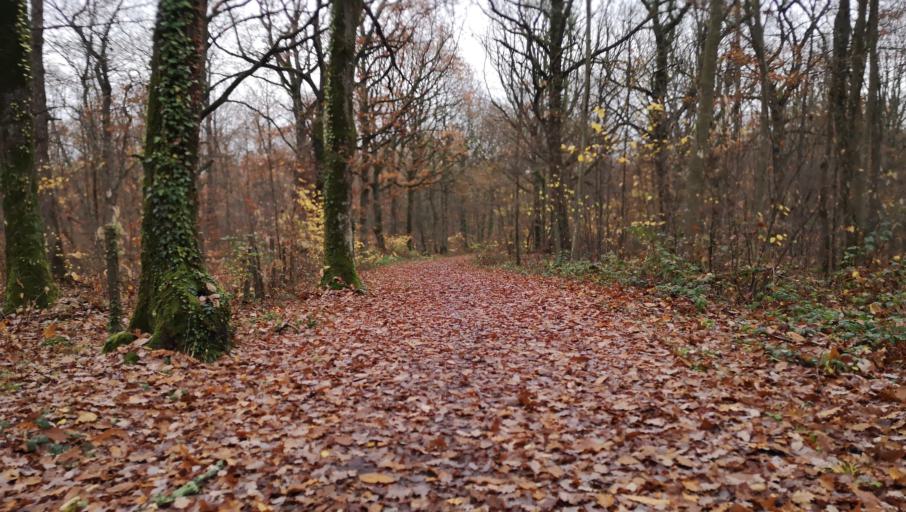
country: FR
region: Centre
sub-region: Departement du Loiret
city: Saint-Jean-de-Braye
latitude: 47.9336
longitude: 1.9840
